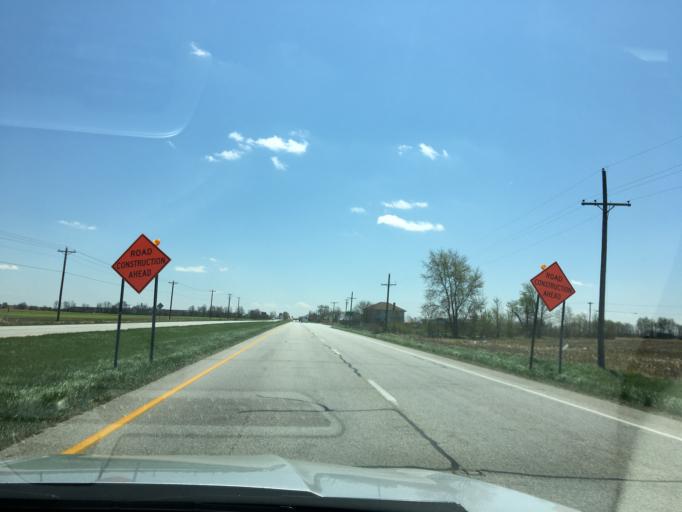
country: US
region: Indiana
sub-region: Clinton County
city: Mulberry
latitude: 40.2600
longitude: -86.7082
